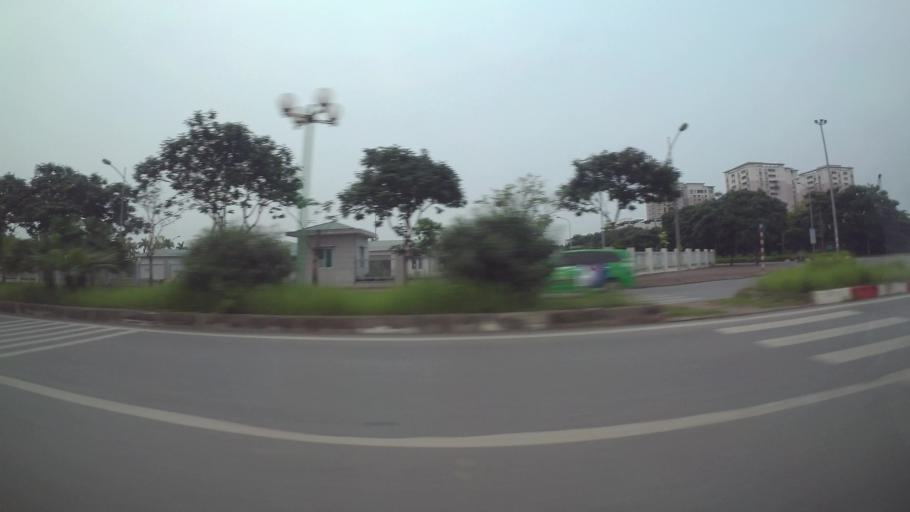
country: VN
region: Ha Noi
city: Trau Quy
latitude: 21.0585
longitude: 105.9038
